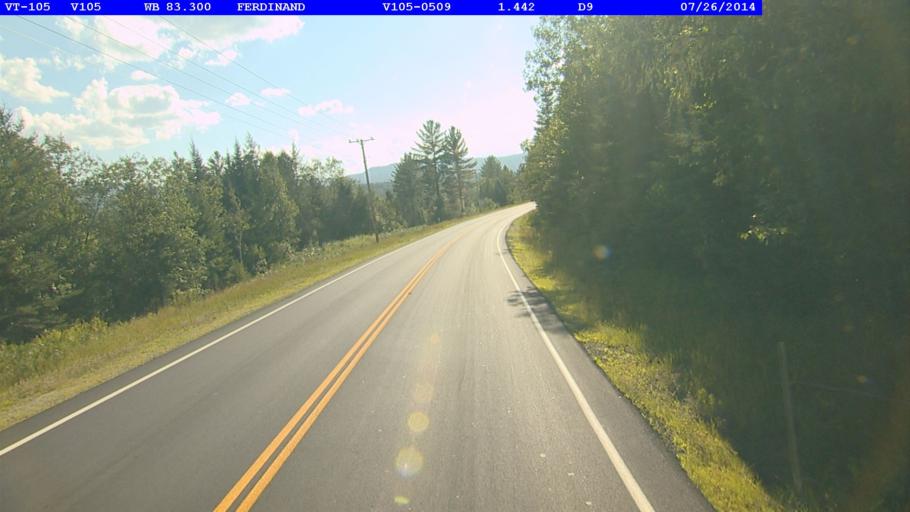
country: US
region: New Hampshire
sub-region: Coos County
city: Stratford
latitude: 44.7795
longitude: -71.7763
